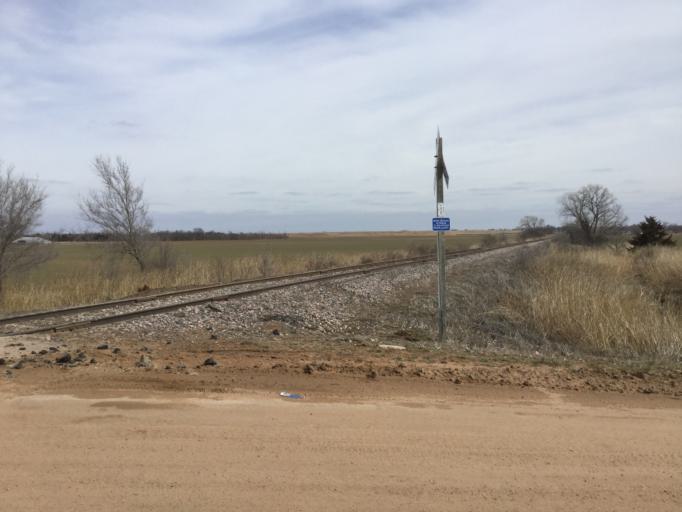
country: US
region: Kansas
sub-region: Barber County
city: Medicine Lodge
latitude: 37.2599
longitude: -98.5687
